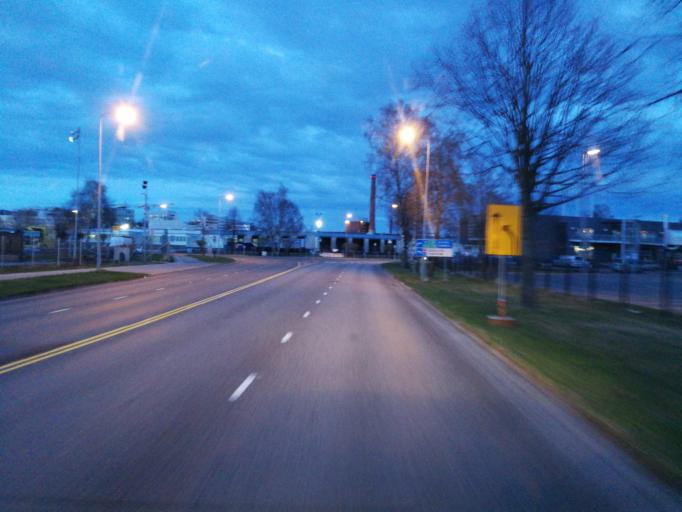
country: FI
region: Varsinais-Suomi
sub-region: Turku
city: Turku
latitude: 60.4410
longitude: 22.2261
